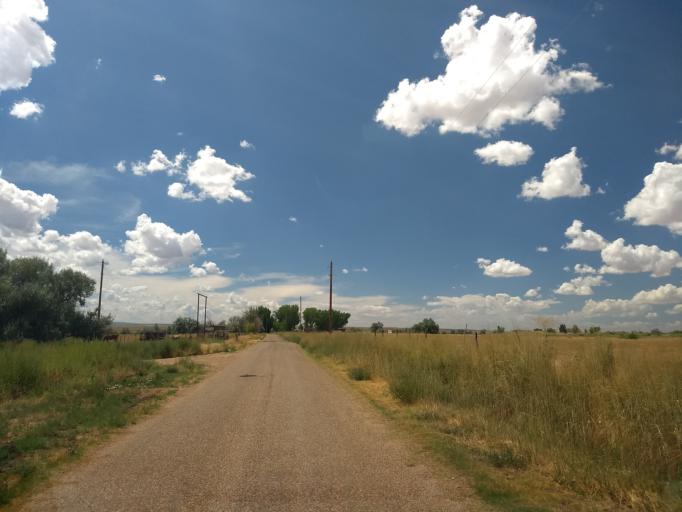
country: US
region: Arizona
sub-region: Coconino County
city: Fredonia
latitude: 36.9422
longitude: -112.5308
